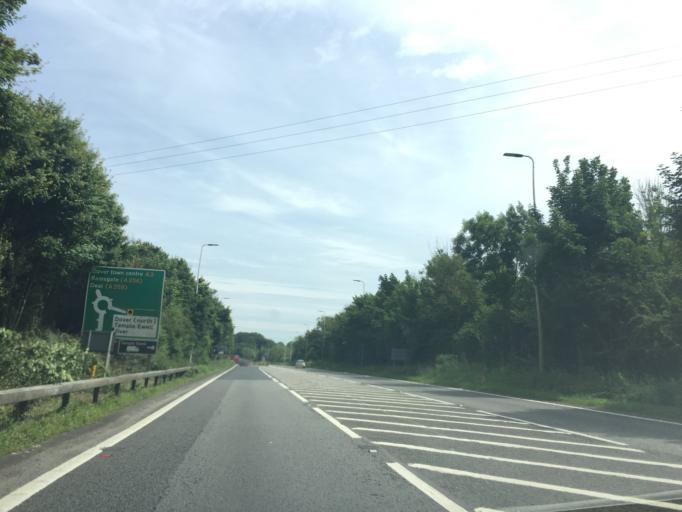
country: GB
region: England
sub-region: Kent
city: Dover
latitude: 51.1566
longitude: 1.2815
